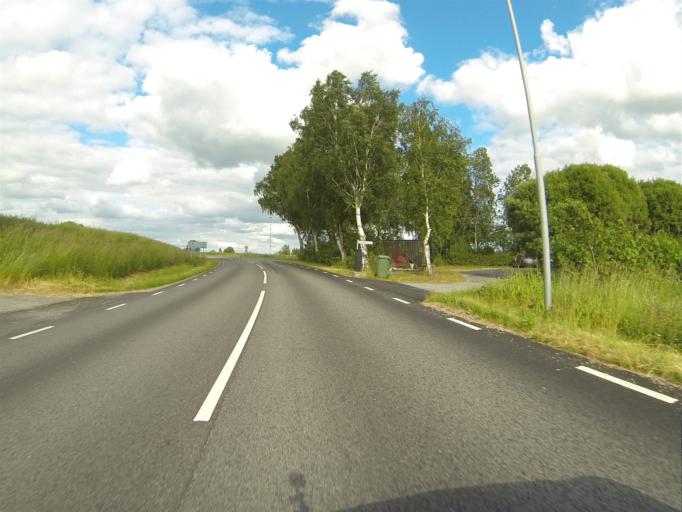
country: SE
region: Skane
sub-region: Staffanstorps Kommun
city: Staffanstorp
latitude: 55.6228
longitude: 13.1951
